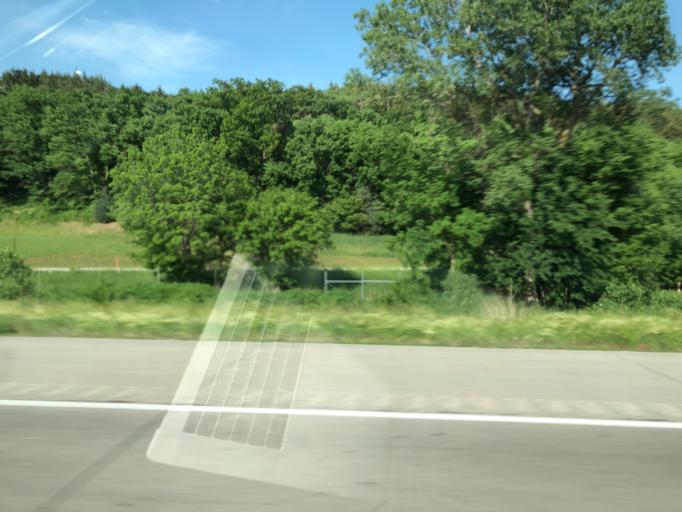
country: US
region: Nebraska
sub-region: Saunders County
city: Ashland
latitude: 41.0432
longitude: -96.2937
